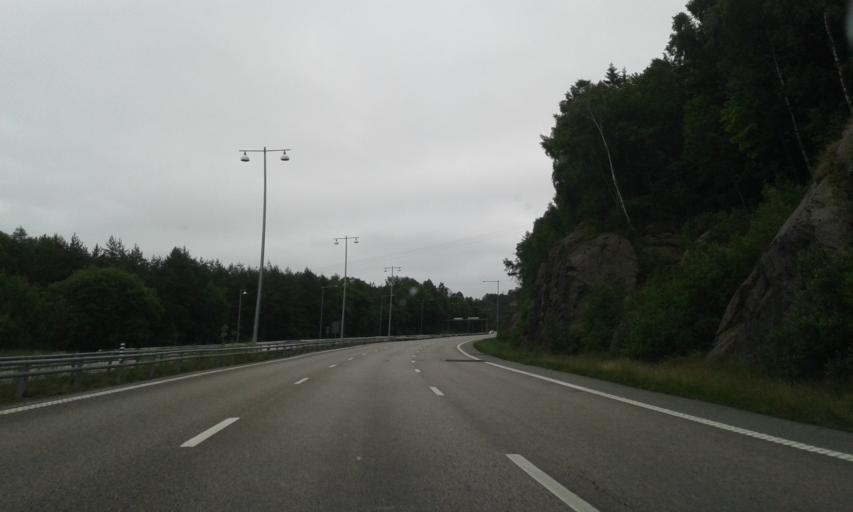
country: SE
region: Vaestra Goetaland
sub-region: Goteborg
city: Hammarkullen
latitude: 57.7884
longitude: 12.0189
